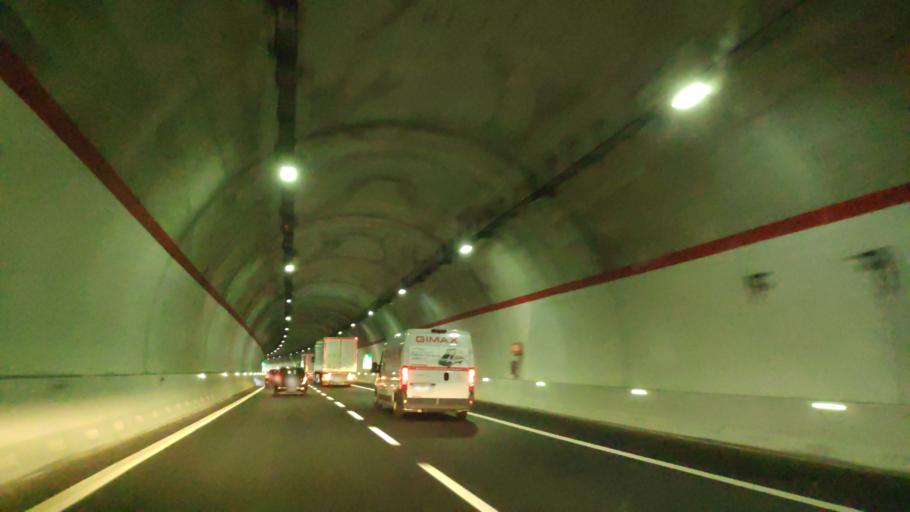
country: IT
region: Campania
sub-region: Provincia di Salerno
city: Casalbuono
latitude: 40.1885
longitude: 15.7074
